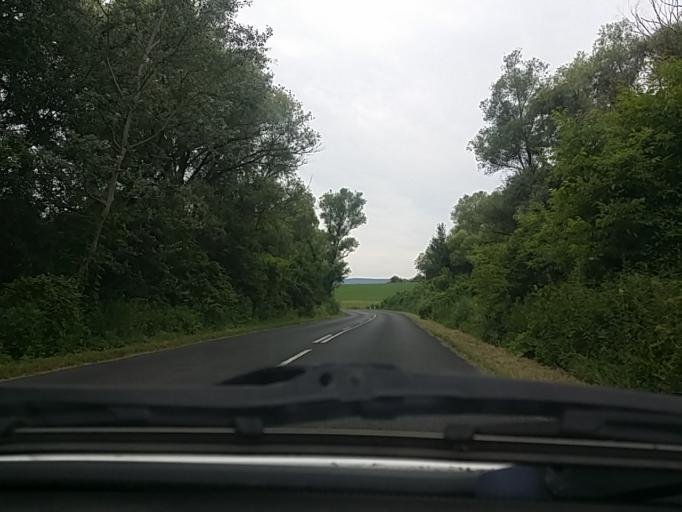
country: HU
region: Pest
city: Csobanka
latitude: 47.6301
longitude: 18.9538
